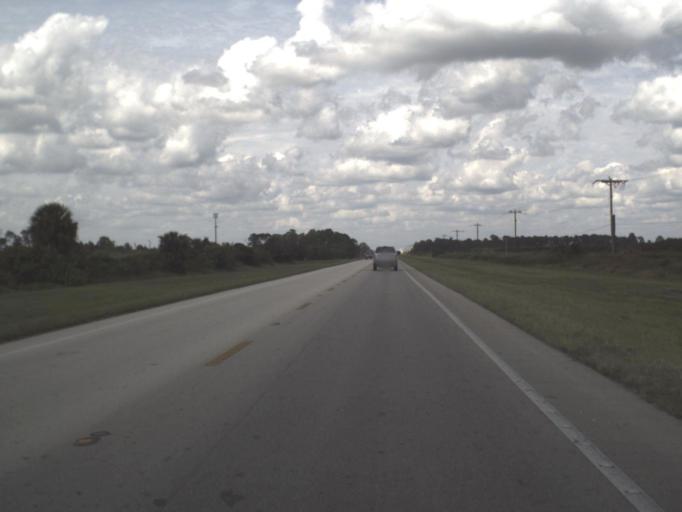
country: US
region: Florida
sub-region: Collier County
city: Immokalee
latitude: 26.4540
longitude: -81.4341
